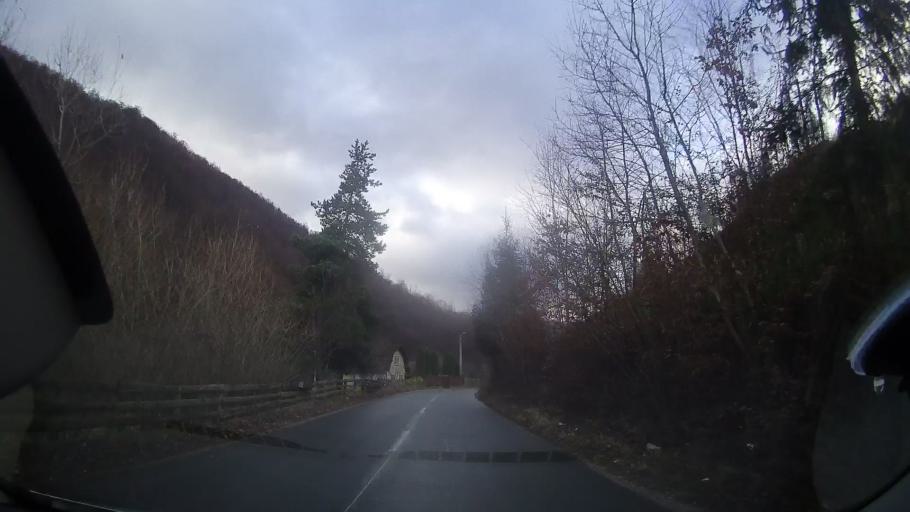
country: RO
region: Cluj
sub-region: Comuna Maguri-Racatau
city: Maguri-Racatau
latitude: 46.6811
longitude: 23.2643
